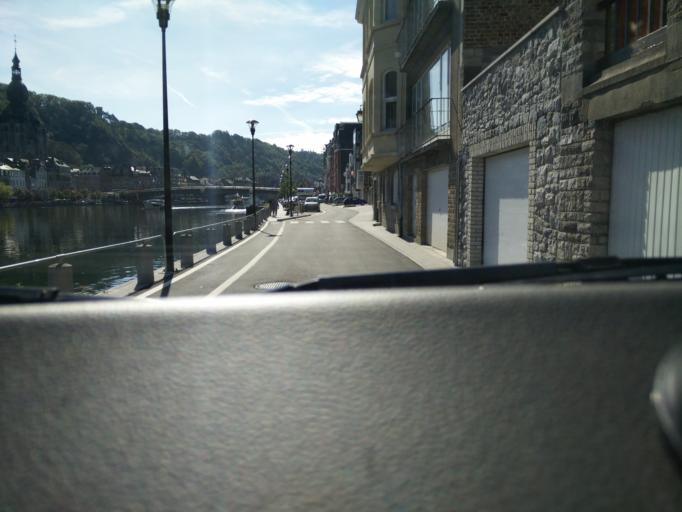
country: BE
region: Wallonia
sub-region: Province de Namur
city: Dinant
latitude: 50.2621
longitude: 4.9080
